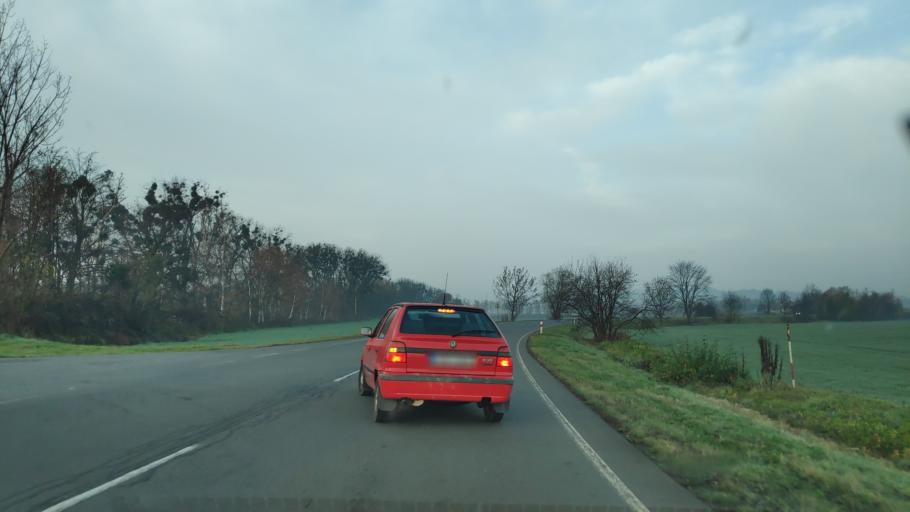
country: CZ
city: Sviadnov
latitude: 49.6910
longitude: 18.3127
